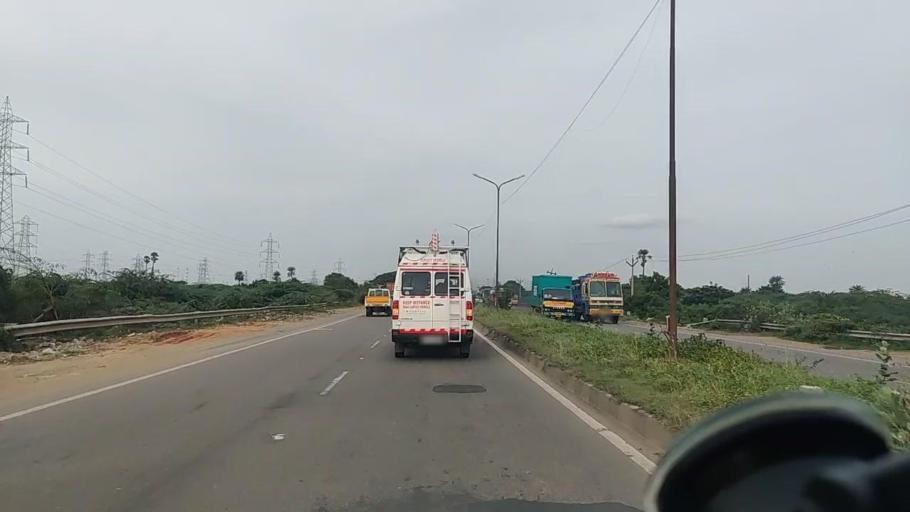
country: IN
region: Tamil Nadu
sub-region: Thiruvallur
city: Chinnasekkadu
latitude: 13.1732
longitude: 80.2361
